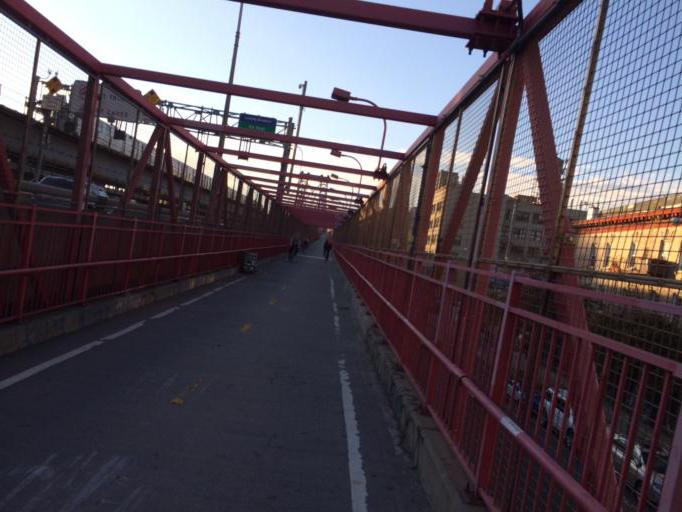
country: US
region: New York
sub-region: Queens County
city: Long Island City
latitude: 40.7116
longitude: -73.9648
